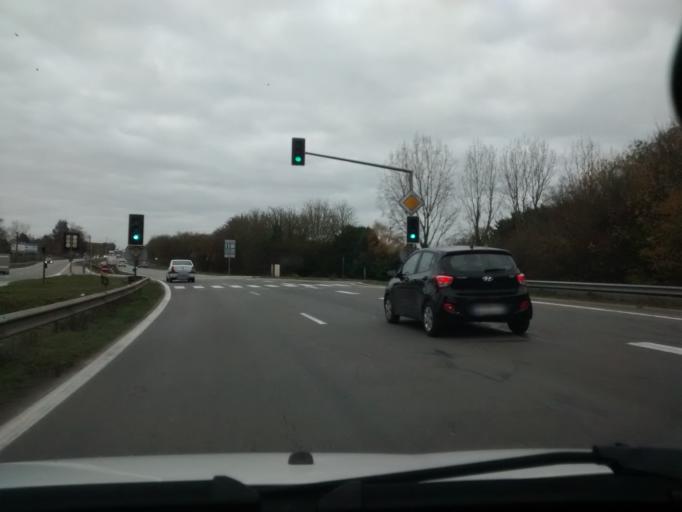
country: FR
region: Brittany
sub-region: Departement d'Ille-et-Vilaine
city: Vezin-le-Coquet
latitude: 48.1046
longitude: -1.7497
